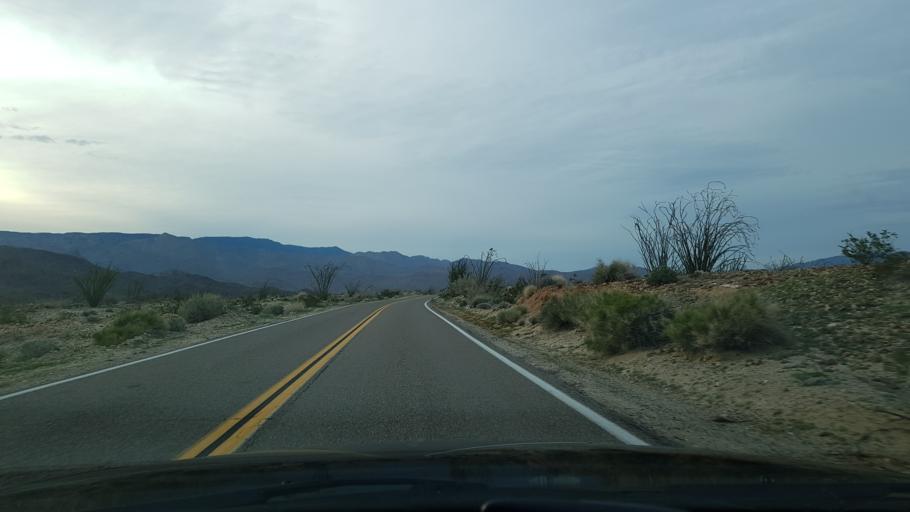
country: MX
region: Baja California
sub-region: Tecate
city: Cereso del Hongo
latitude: 32.8229
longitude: -116.1592
